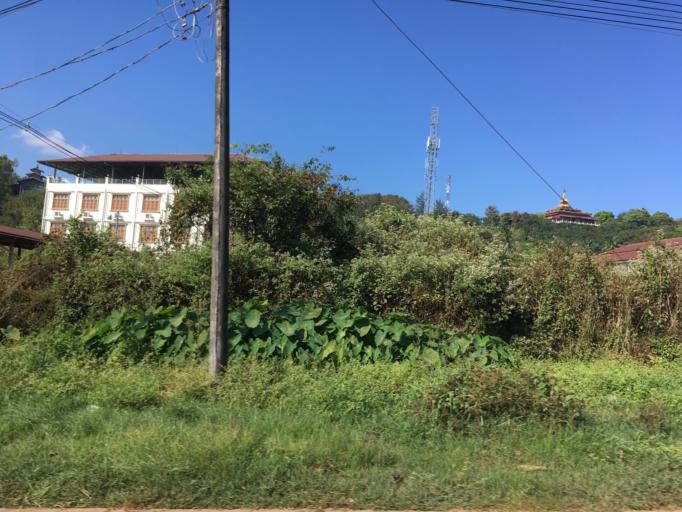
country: MM
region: Mon
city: Mawlamyine
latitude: 16.4770
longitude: 97.6332
